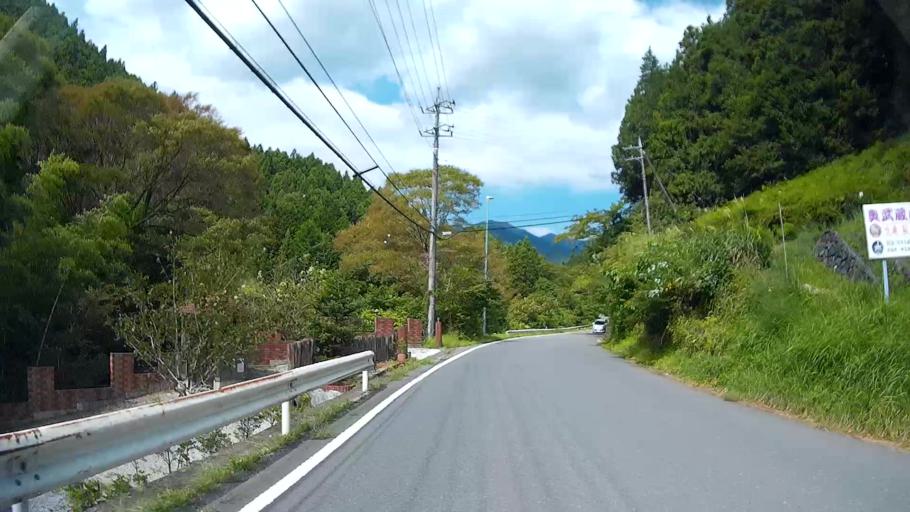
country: JP
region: Saitama
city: Chichibu
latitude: 35.9065
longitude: 139.1556
